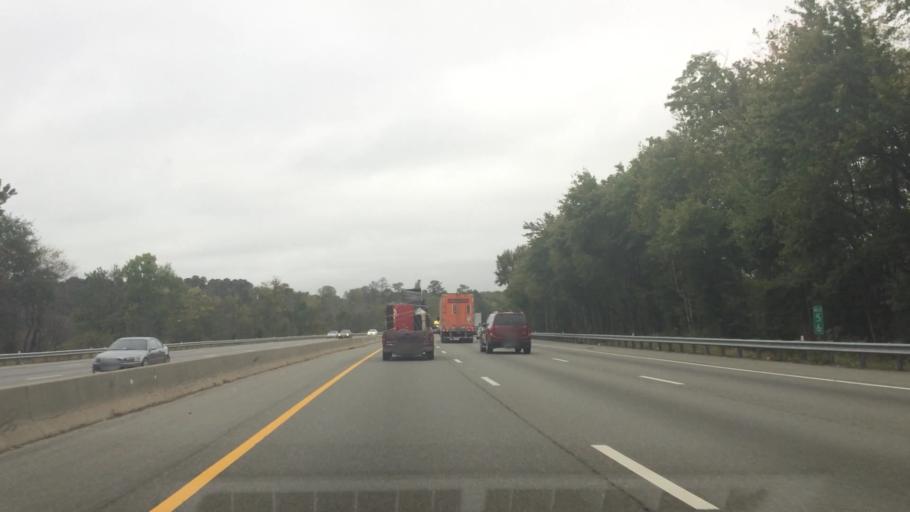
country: US
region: Virginia
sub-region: City of Colonial Heights
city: Colonial Heights
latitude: 37.2803
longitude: -77.3891
